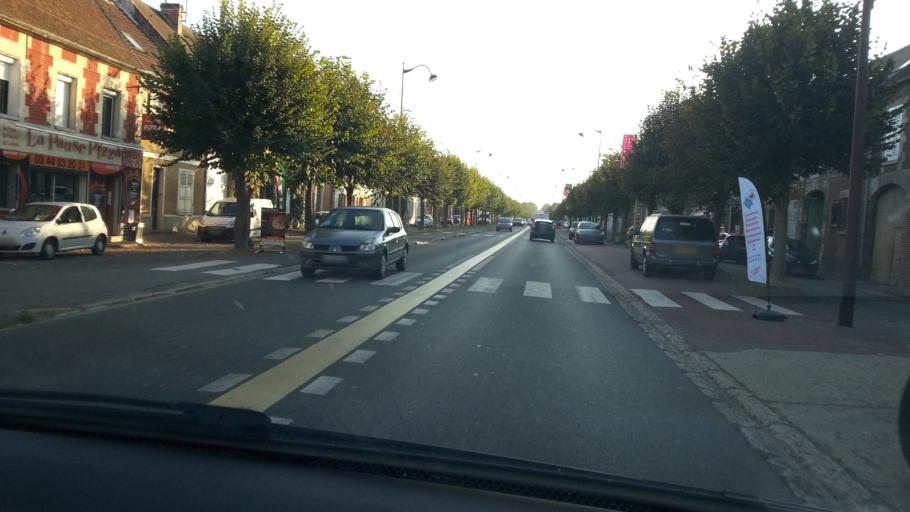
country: FR
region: Picardie
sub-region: Departement de l'Oise
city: Estrees-Saint-Denis
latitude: 49.4264
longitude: 2.6378
